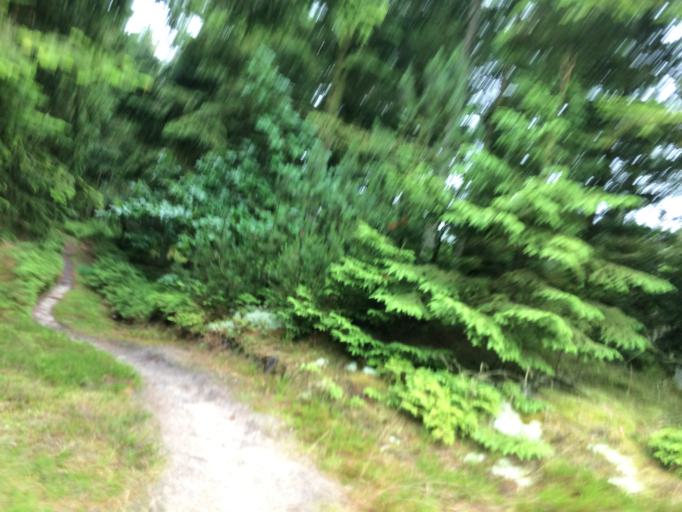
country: DK
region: Central Jutland
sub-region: Holstebro Kommune
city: Ulfborg
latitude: 56.2477
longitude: 8.4438
